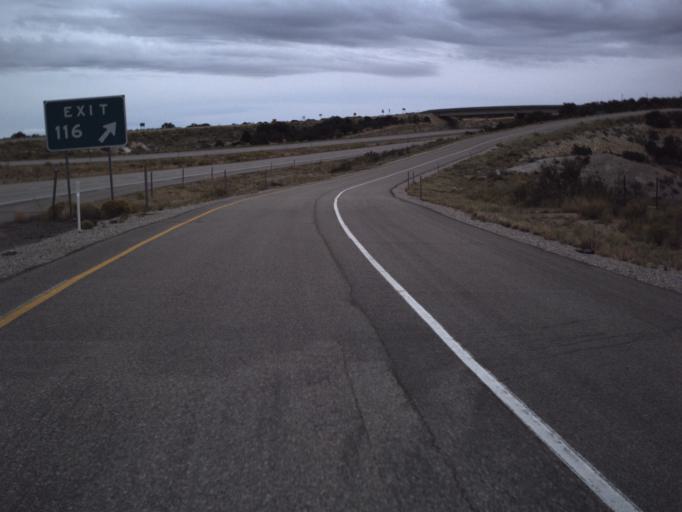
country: US
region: Utah
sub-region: Emery County
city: Ferron
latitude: 38.8551
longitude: -110.9201
